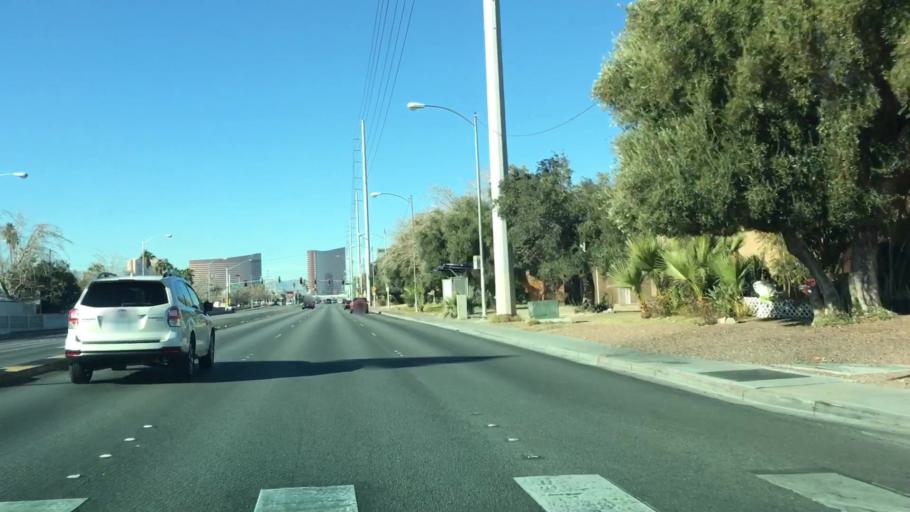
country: US
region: Nevada
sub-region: Clark County
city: Winchester
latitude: 36.1299
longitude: -115.1323
